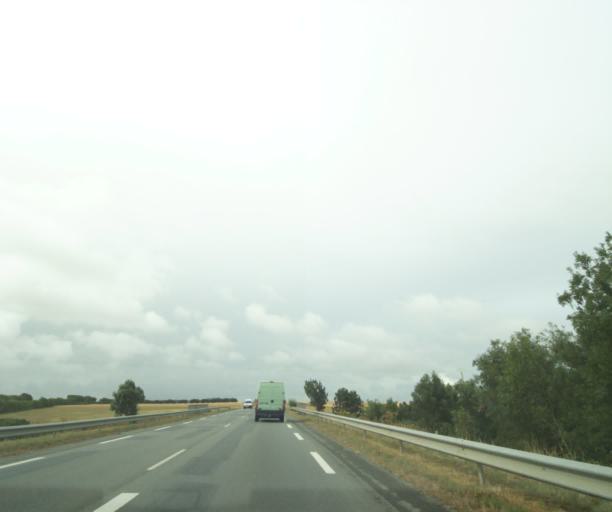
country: FR
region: Poitou-Charentes
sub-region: Departement de la Charente-Maritime
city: Lagord
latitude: 46.2056
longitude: -1.1375
